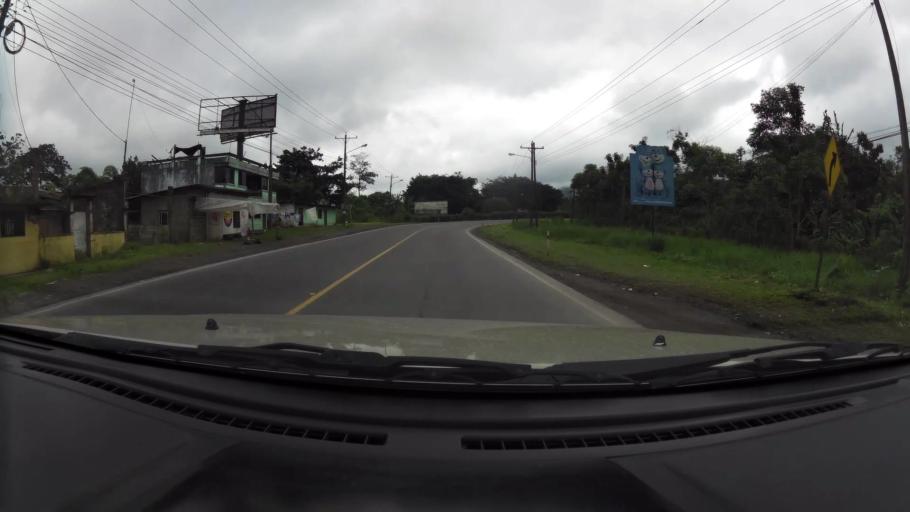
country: EC
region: Santo Domingo de los Tsachilas
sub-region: Canton Santo Domingo de los Colorados
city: Santo Domingo de los Colorados
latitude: -0.2641
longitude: -79.1121
